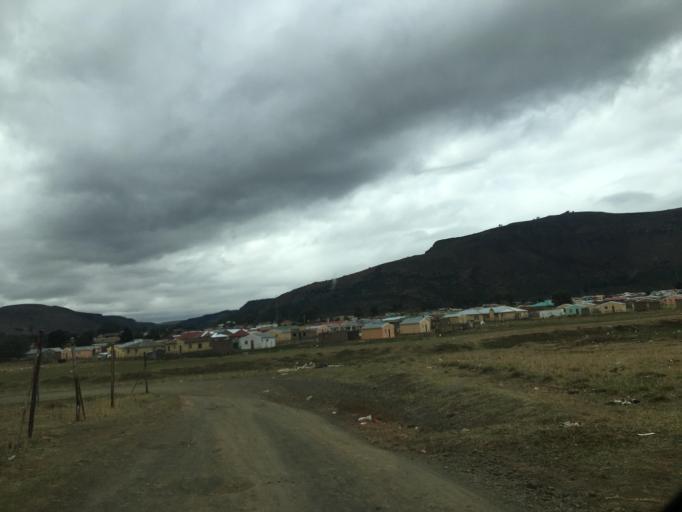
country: ZA
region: Eastern Cape
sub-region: Chris Hani District Municipality
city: Cala
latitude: -31.5347
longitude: 27.6949
